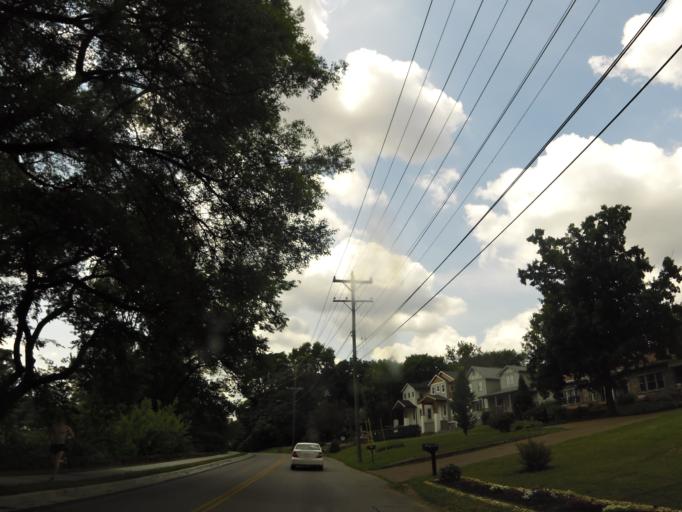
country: US
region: Tennessee
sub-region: Davidson County
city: Oak Hill
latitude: 36.1200
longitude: -86.7877
